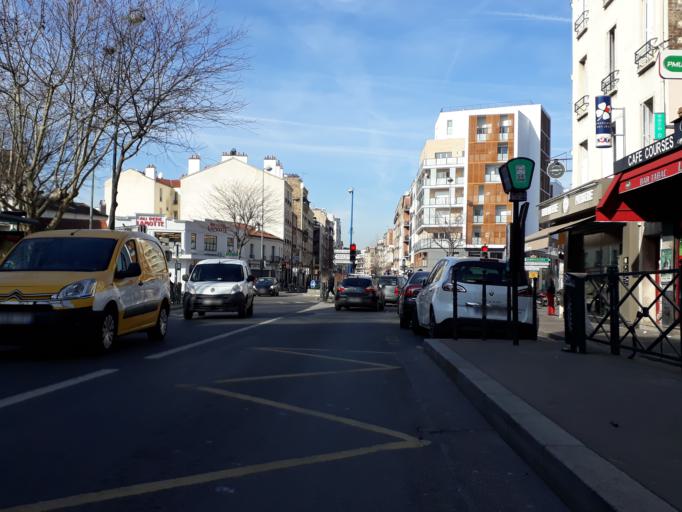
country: FR
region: Ile-de-France
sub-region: Departement des Hauts-de-Seine
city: Asnieres-sur-Seine
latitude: 48.9122
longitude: 2.2965
